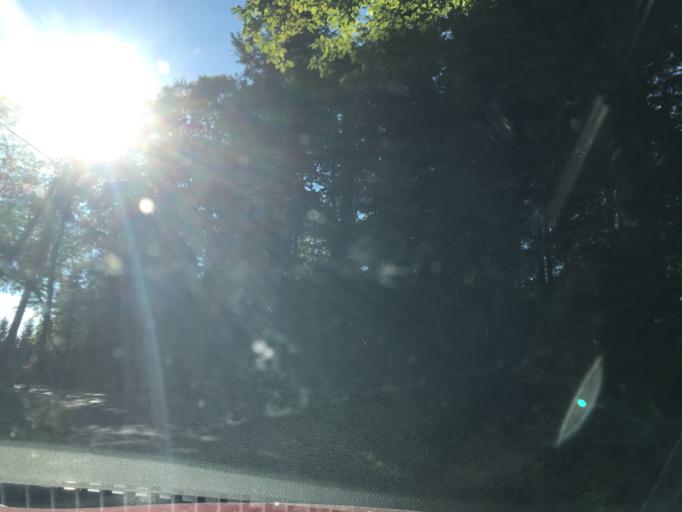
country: FR
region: Auvergne
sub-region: Departement du Puy-de-Dome
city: Escoutoux
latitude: 45.7733
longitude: 3.6148
